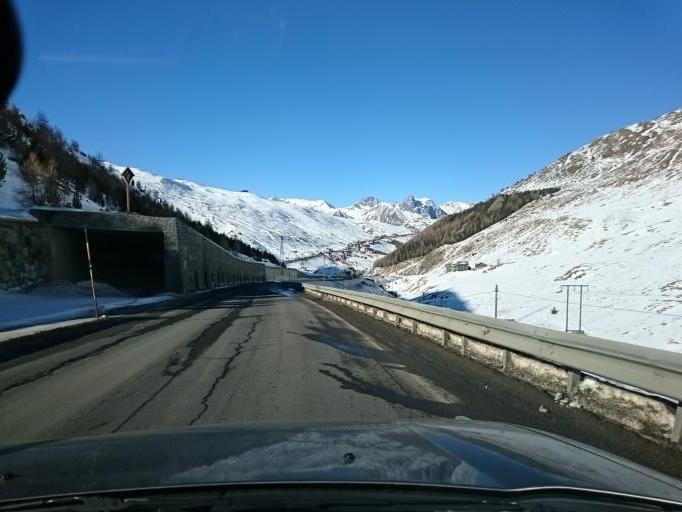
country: IT
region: Lombardy
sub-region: Provincia di Sondrio
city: Livigno
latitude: 46.5127
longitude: 10.1945
